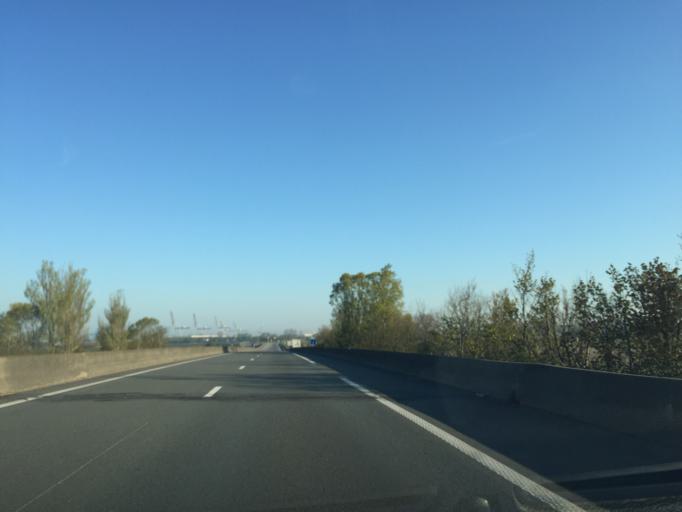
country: FR
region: Nord-Pas-de-Calais
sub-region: Departement du Nord
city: Loon-Plage
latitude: 50.9874
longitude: 2.2067
